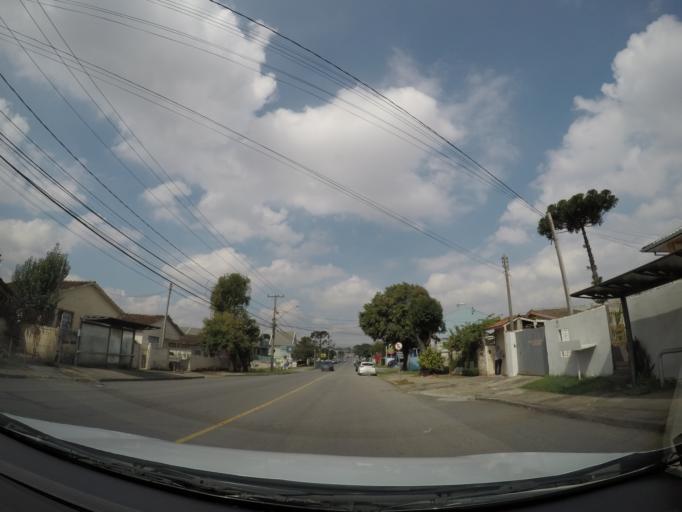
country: BR
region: Parana
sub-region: Sao Jose Dos Pinhais
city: Sao Jose dos Pinhais
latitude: -25.4872
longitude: -49.2514
